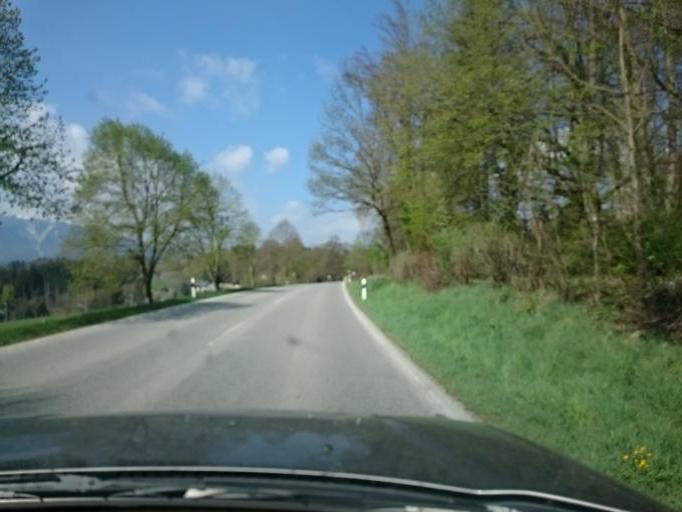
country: DE
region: Bavaria
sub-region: Upper Bavaria
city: Seehausen am Staffelsee
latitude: 47.6725
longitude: 11.1731
